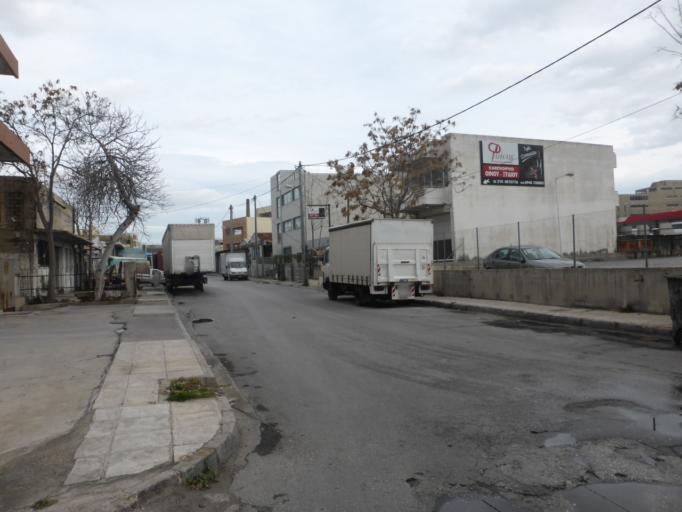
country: GR
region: Attica
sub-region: Nomarchia Athinas
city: Tavros
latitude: 37.9603
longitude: 23.6848
